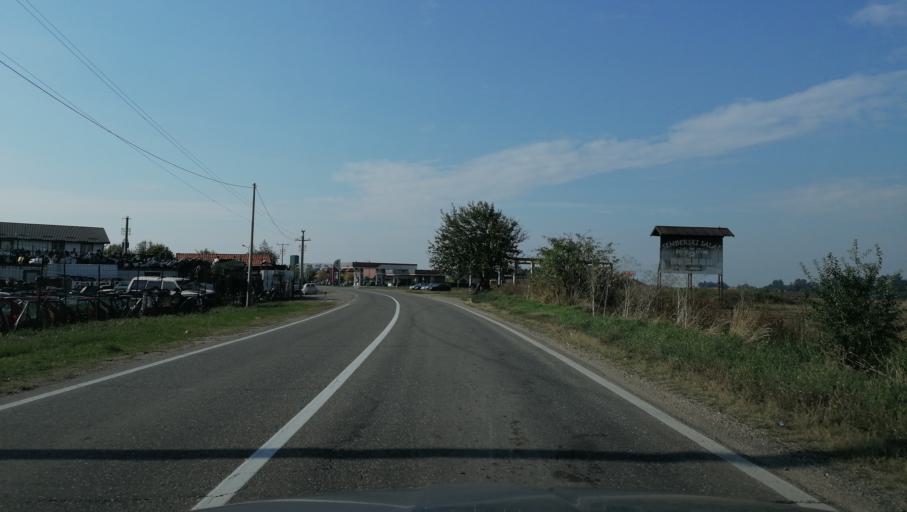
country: BA
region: Republika Srpska
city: Popovi
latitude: 44.7850
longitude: 19.2813
